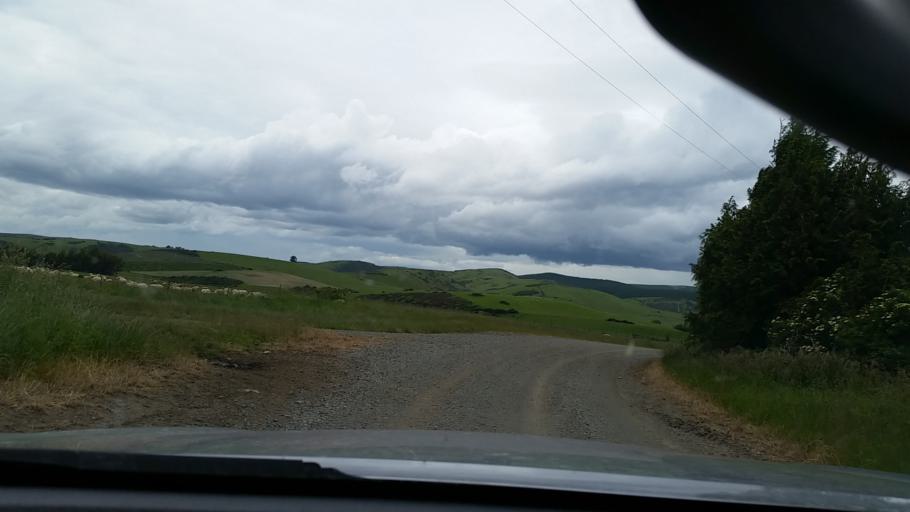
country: NZ
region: Southland
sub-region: Southland District
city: Winton
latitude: -45.8511
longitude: 168.1394
